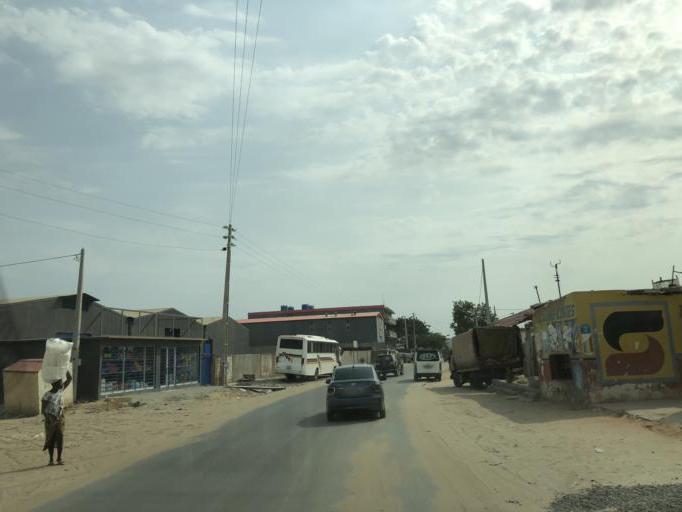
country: AO
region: Luanda
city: Luanda
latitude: -8.9021
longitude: 13.3479
